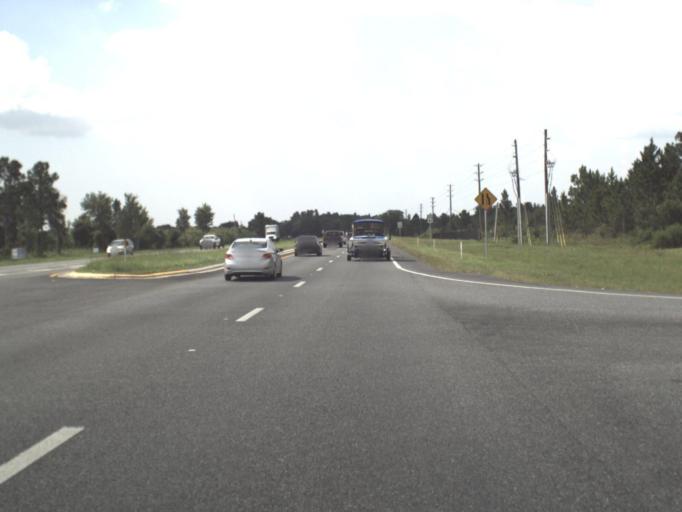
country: US
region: Florida
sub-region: Pasco County
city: Land O' Lakes
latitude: 28.2887
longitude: -82.4882
